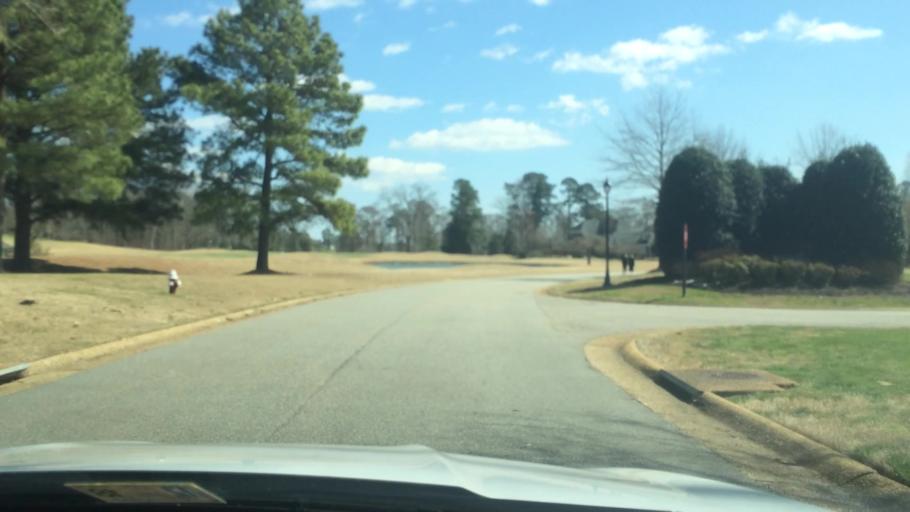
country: US
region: Virginia
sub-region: City of Williamsburg
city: Williamsburg
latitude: 37.2286
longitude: -76.6789
